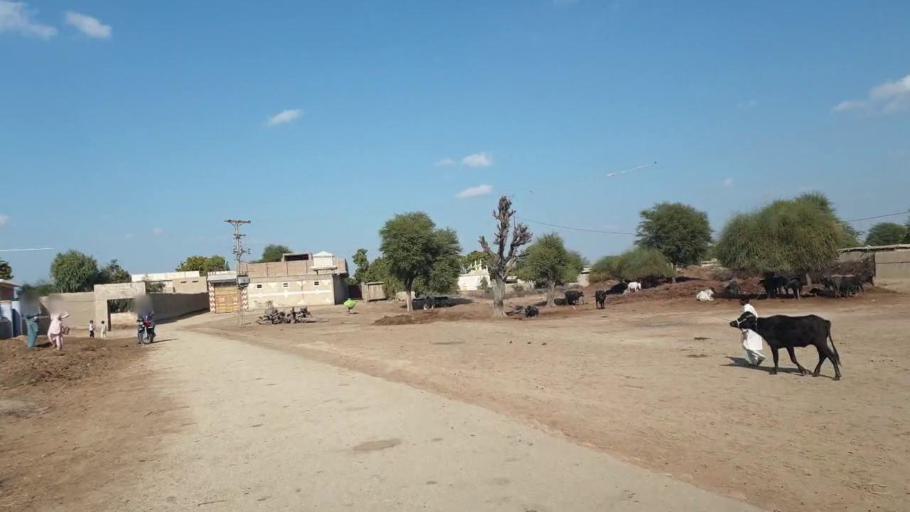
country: PK
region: Sindh
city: Shahpur Chakar
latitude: 26.1023
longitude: 68.5750
